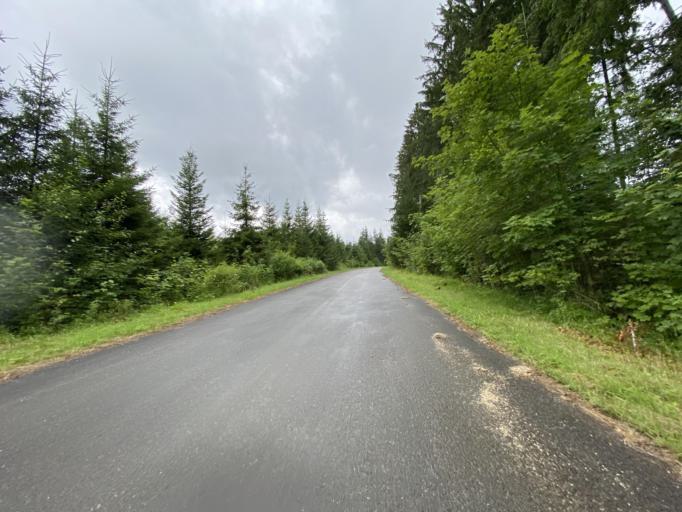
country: DE
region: Baden-Wuerttemberg
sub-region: Tuebingen Region
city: Sigmaringen
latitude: 48.1147
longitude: 9.2418
